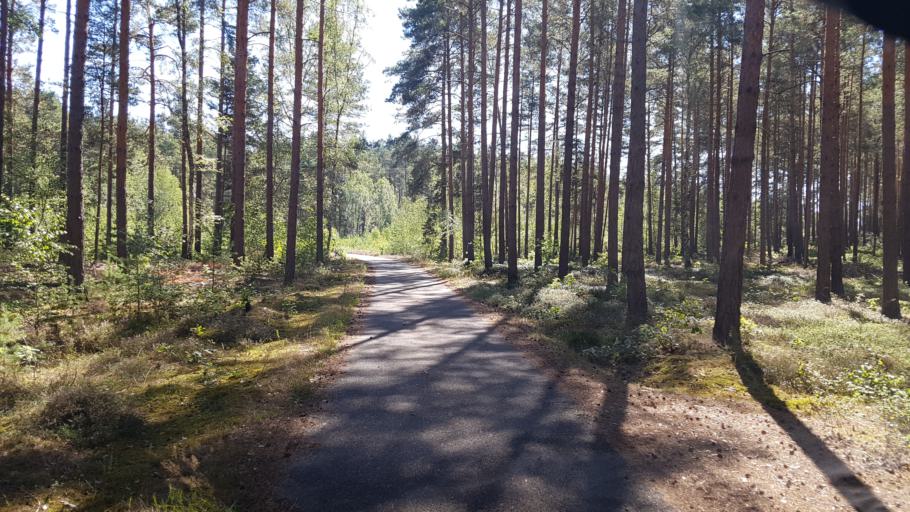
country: DE
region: Brandenburg
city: Calau
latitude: 51.7096
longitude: 13.9949
